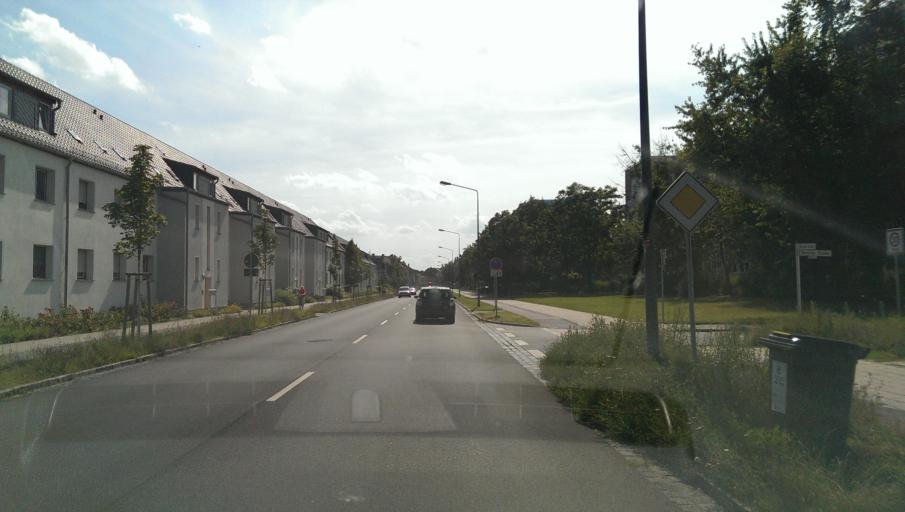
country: DE
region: Saxony-Anhalt
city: Wittenburg
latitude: 51.8775
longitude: 12.6510
